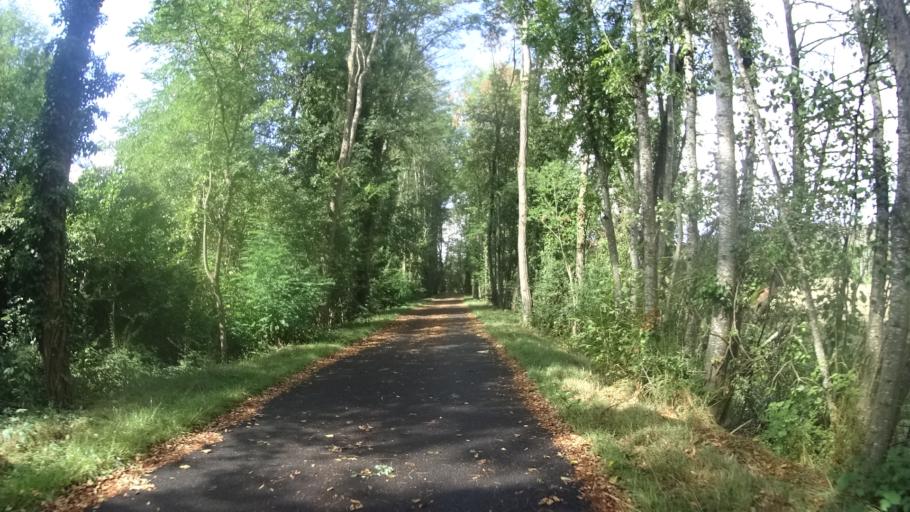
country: FR
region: Bourgogne
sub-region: Departement de Saone-et-Loire
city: Saint-Leger-sur-Dheune
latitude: 46.8158
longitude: 4.5896
